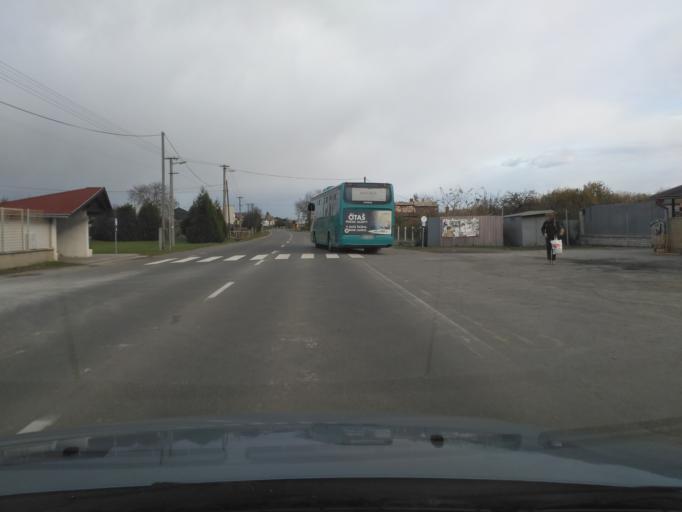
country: HU
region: Borsod-Abauj-Zemplen
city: Satoraljaujhely
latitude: 48.3984
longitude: 21.7418
